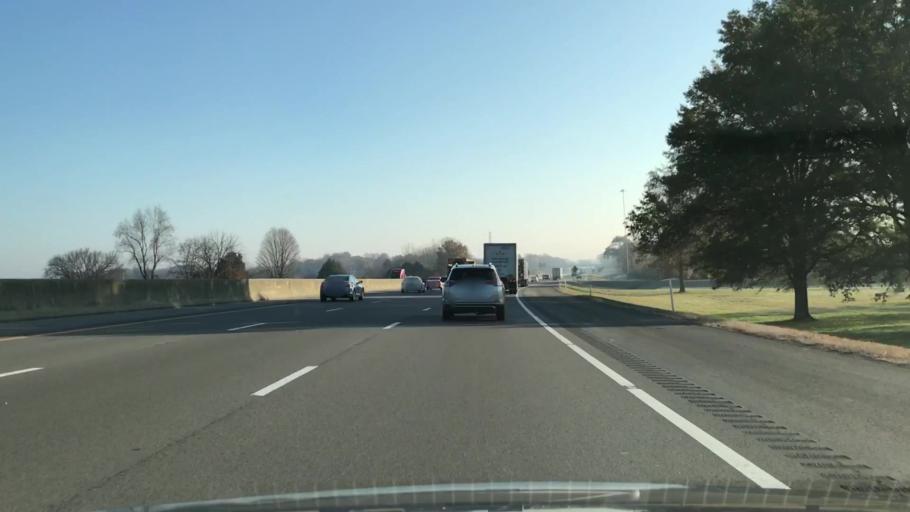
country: US
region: Kentucky
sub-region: Warren County
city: Bowling Green
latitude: 37.0071
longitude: -86.3654
